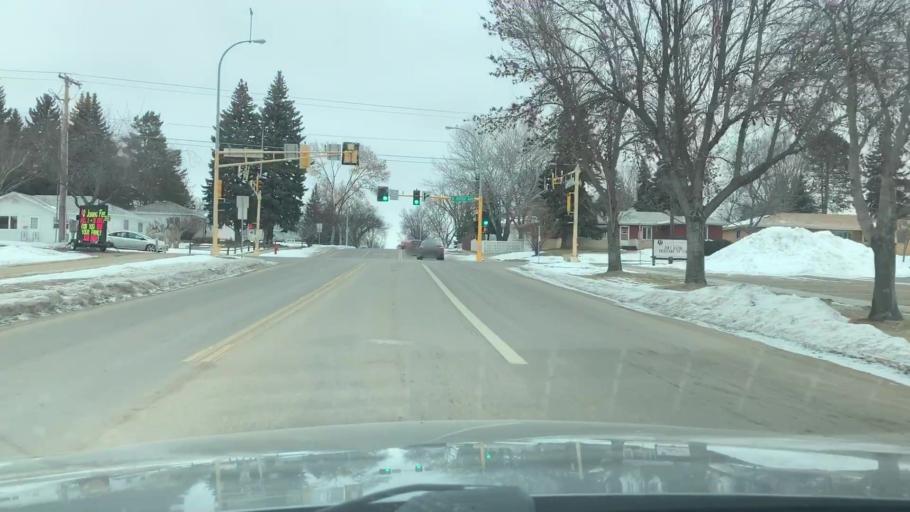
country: US
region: North Dakota
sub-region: Burleigh County
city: Bismarck
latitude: 46.8232
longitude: -100.7941
